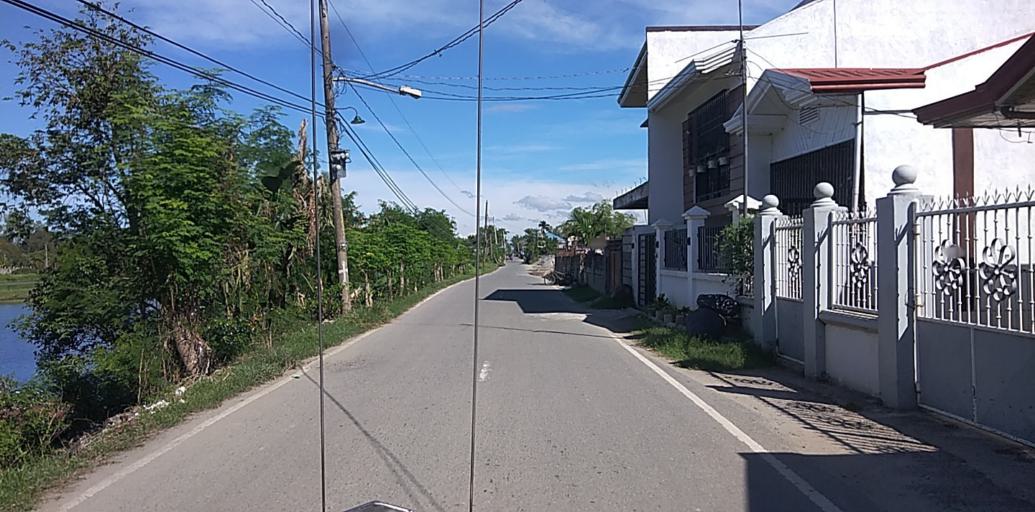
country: PH
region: Central Luzon
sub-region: Province of Pampanga
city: Candaba
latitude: 15.0965
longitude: 120.8132
